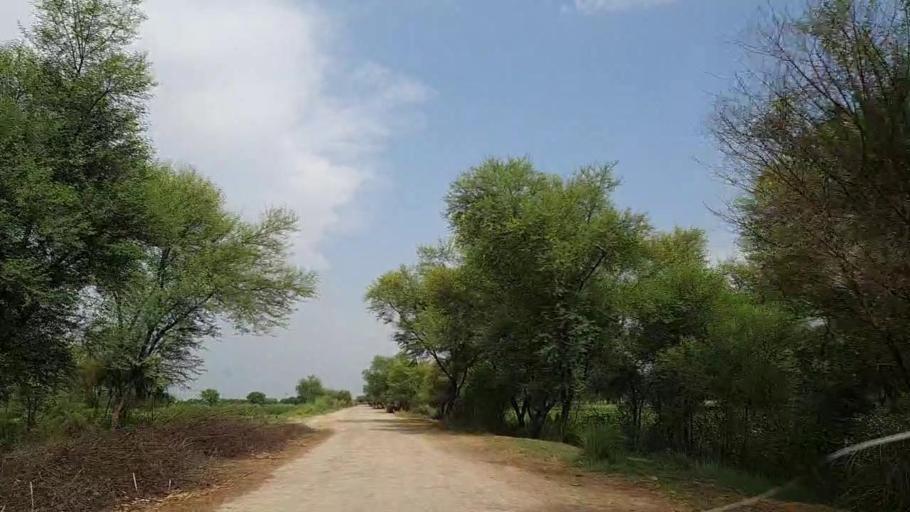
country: PK
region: Sindh
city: Khanpur
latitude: 27.8381
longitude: 69.4885
